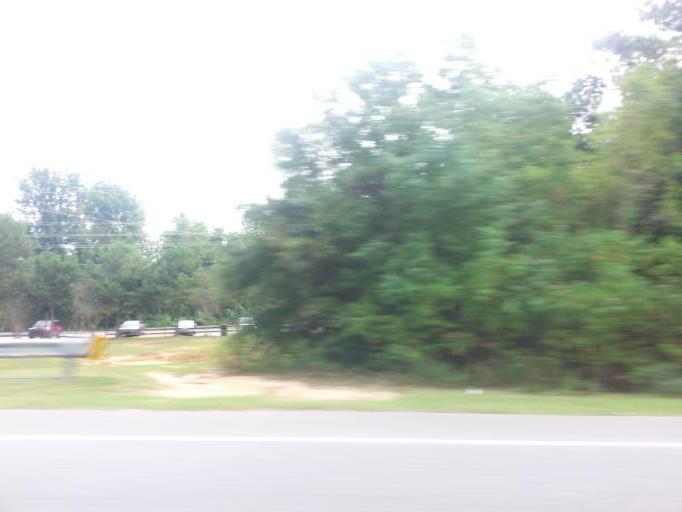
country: US
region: Alabama
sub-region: Baldwin County
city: Spanish Fort
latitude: 30.6514
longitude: -87.9123
